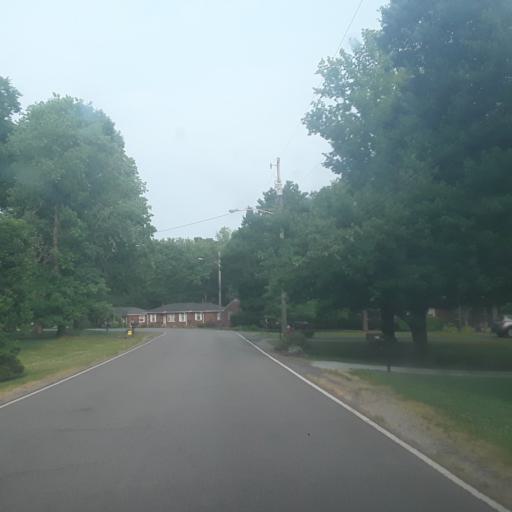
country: US
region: Tennessee
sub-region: Davidson County
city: Oak Hill
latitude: 36.0674
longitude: -86.7542
